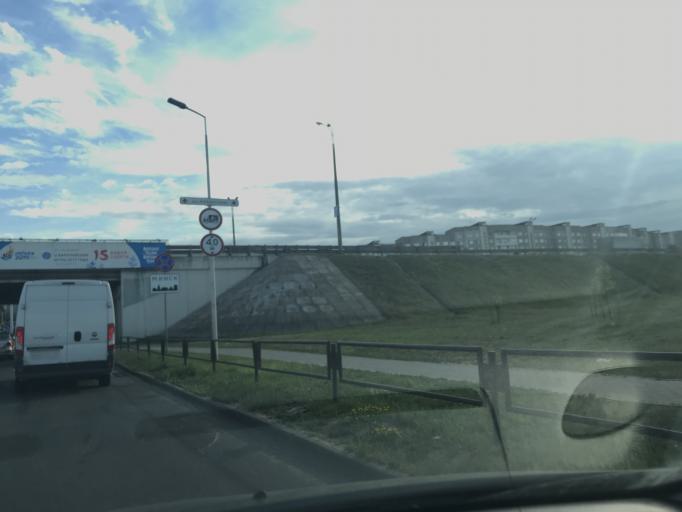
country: BY
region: Minsk
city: Bal'shavik
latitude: 53.9631
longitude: 27.6192
